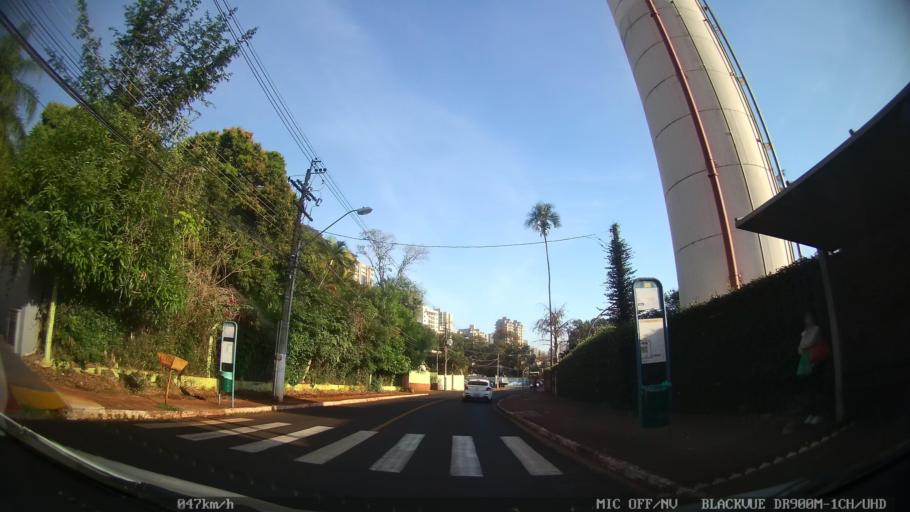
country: BR
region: Sao Paulo
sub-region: Ribeirao Preto
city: Ribeirao Preto
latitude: -21.2095
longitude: -47.7916
